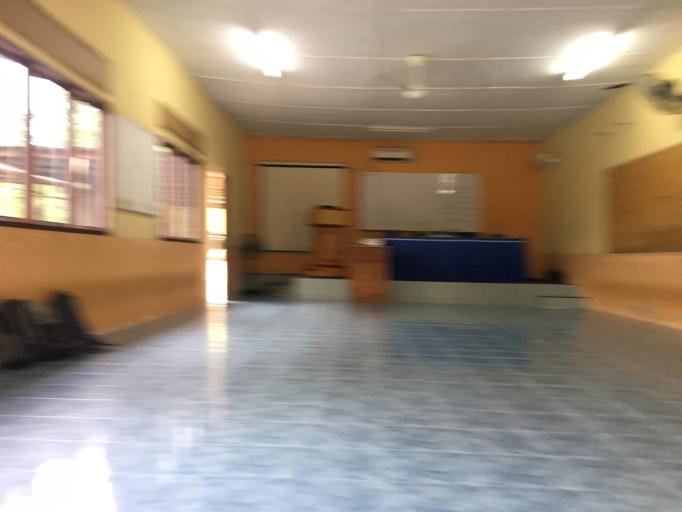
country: MY
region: Perak
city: Lumut
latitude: 4.2990
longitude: 100.6710
